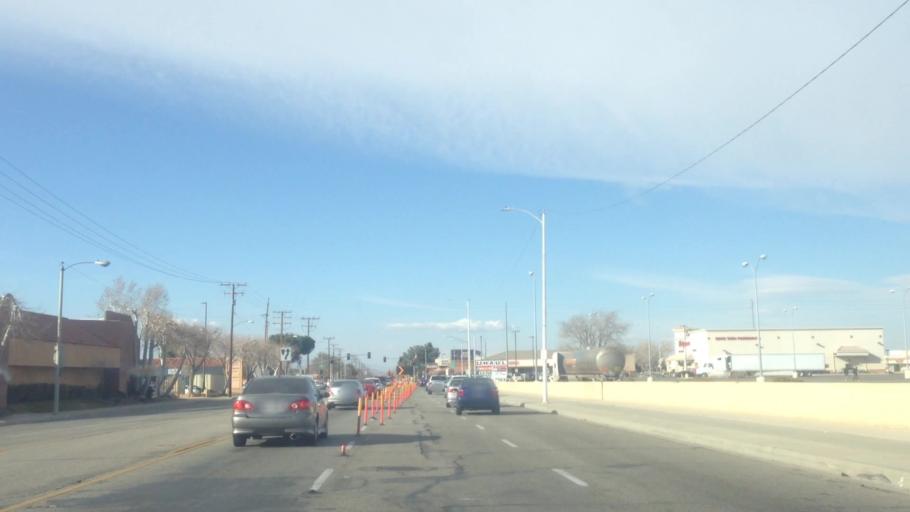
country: US
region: California
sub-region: Los Angeles County
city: Lancaster
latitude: 34.6873
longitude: -118.1656
